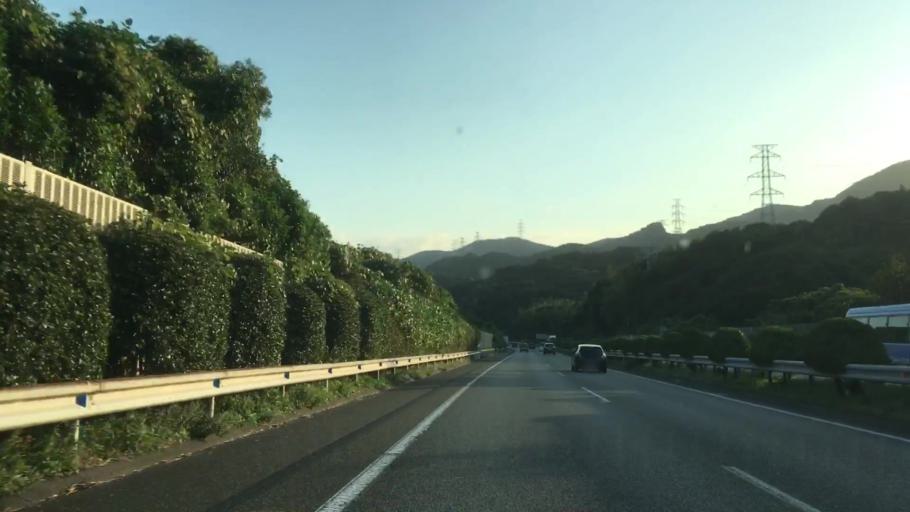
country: JP
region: Yamaguchi
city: Shimonoseki
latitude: 33.9083
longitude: 130.9741
